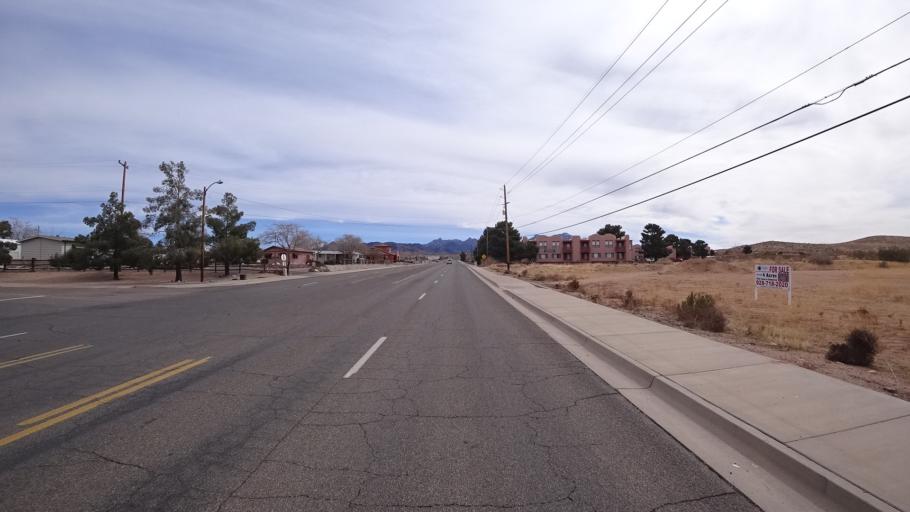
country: US
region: Arizona
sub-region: Mohave County
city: Kingman
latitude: 35.1890
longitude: -114.0120
